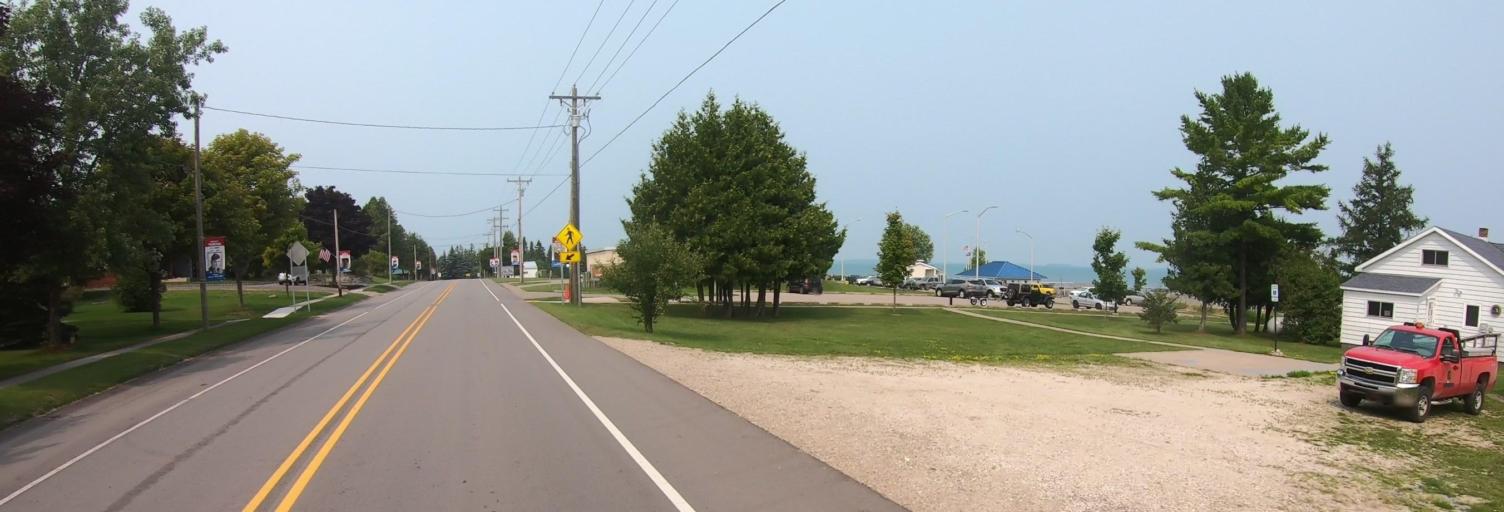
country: CA
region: Ontario
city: Thessalon
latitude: 45.9973
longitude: -83.9018
